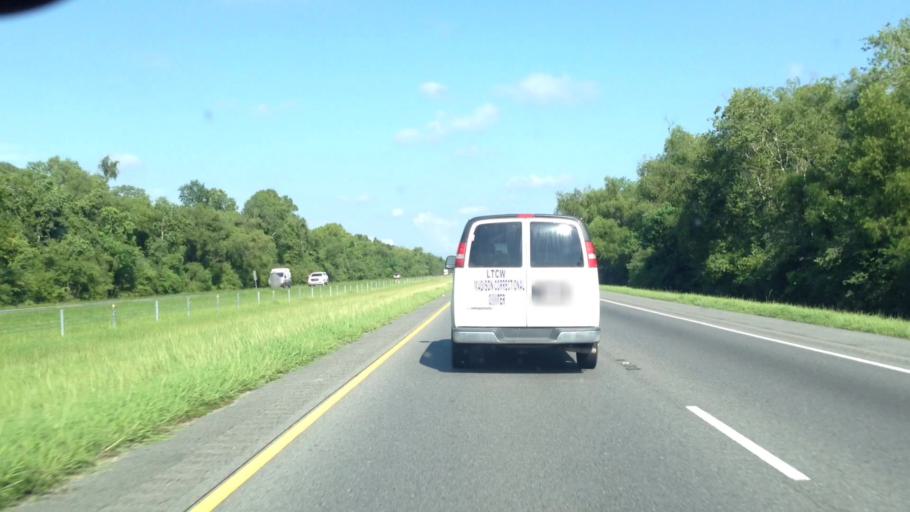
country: US
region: Louisiana
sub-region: Saint James Parish
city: Grand Point
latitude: 30.1339
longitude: -90.7270
